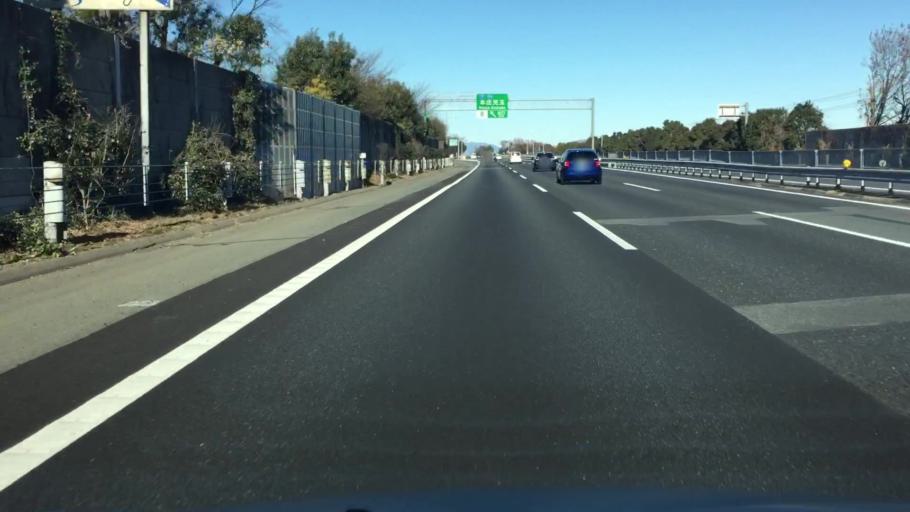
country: JP
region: Saitama
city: Honjo
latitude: 36.2143
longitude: 139.1672
